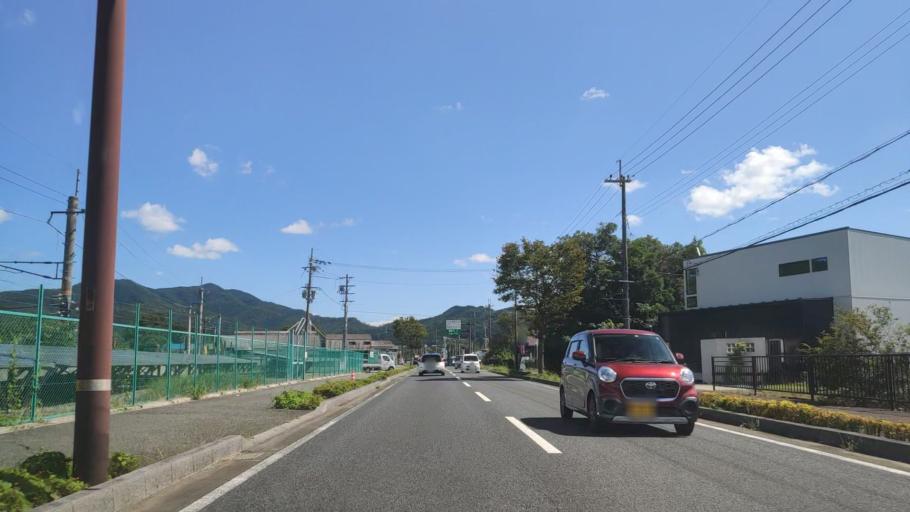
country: JP
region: Kyoto
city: Fukuchiyama
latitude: 35.1666
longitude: 135.1099
